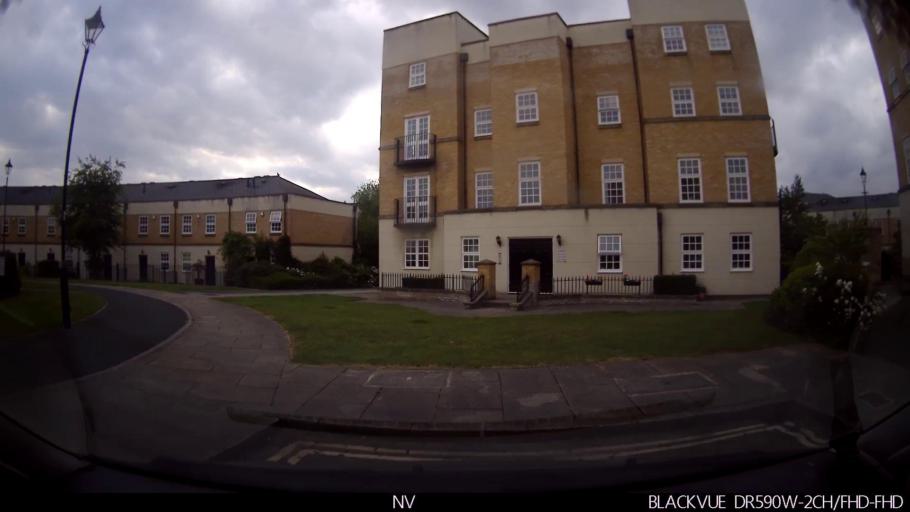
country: GB
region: England
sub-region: City of York
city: York
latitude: 53.9603
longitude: -1.1011
